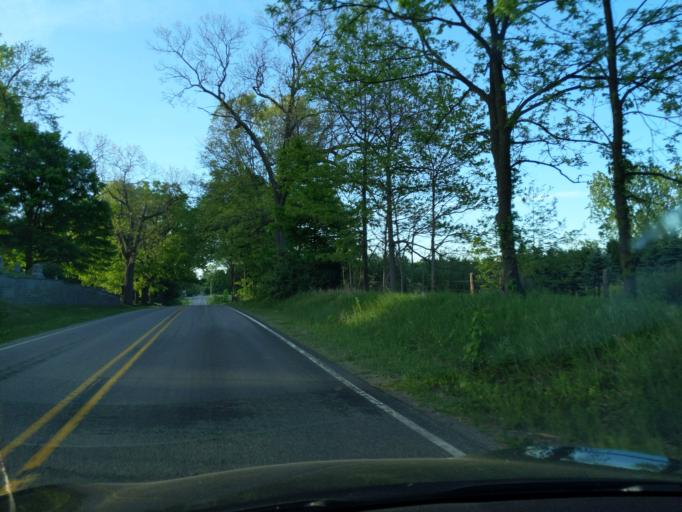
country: US
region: Michigan
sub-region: Ingham County
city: Leslie
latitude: 42.4718
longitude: -84.3169
